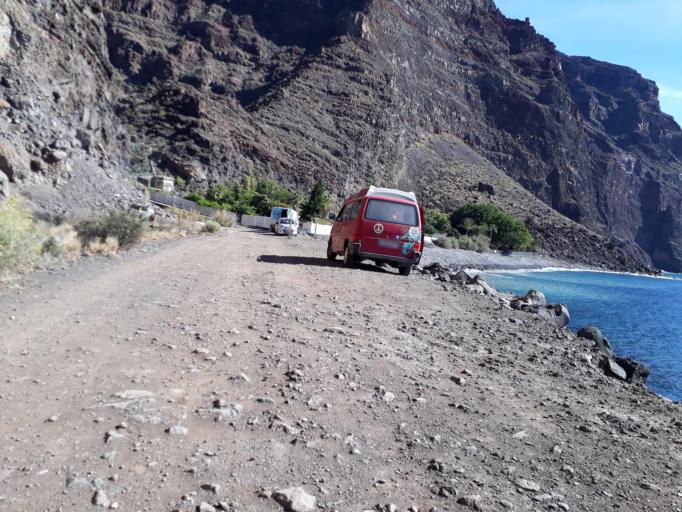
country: ES
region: Canary Islands
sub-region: Provincia de Santa Cruz de Tenerife
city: Alajero
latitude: 28.0803
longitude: -17.3252
